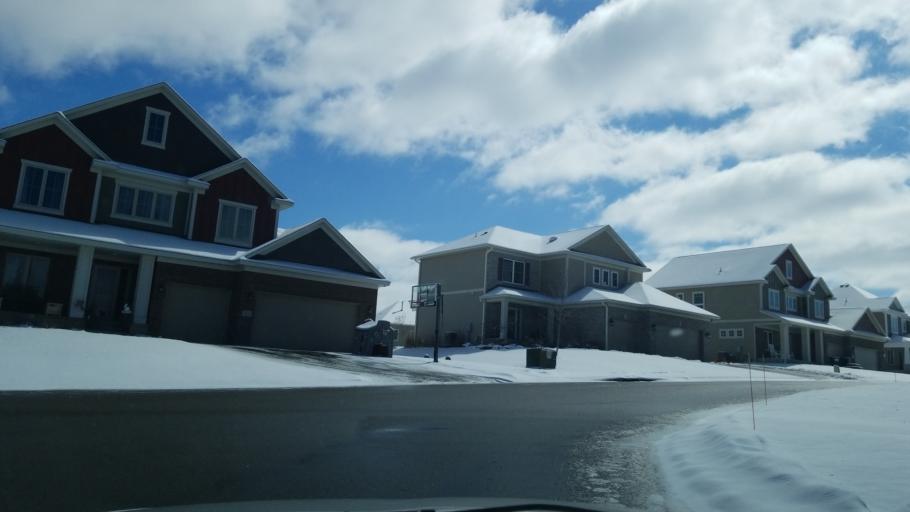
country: US
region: Wisconsin
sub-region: Saint Croix County
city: Hudson
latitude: 44.9516
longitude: -92.7031
